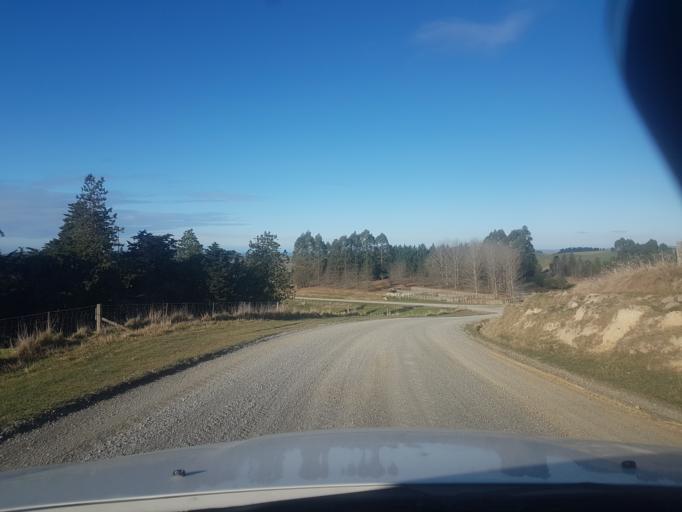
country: NZ
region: Canterbury
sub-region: Timaru District
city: Pleasant Point
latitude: -44.1681
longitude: 170.9175
